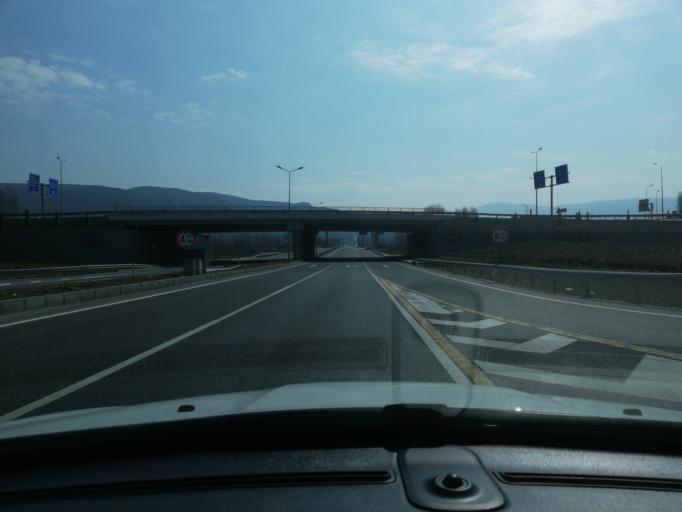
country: TR
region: Cankiri
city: Ilgaz
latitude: 40.9054
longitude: 33.6493
